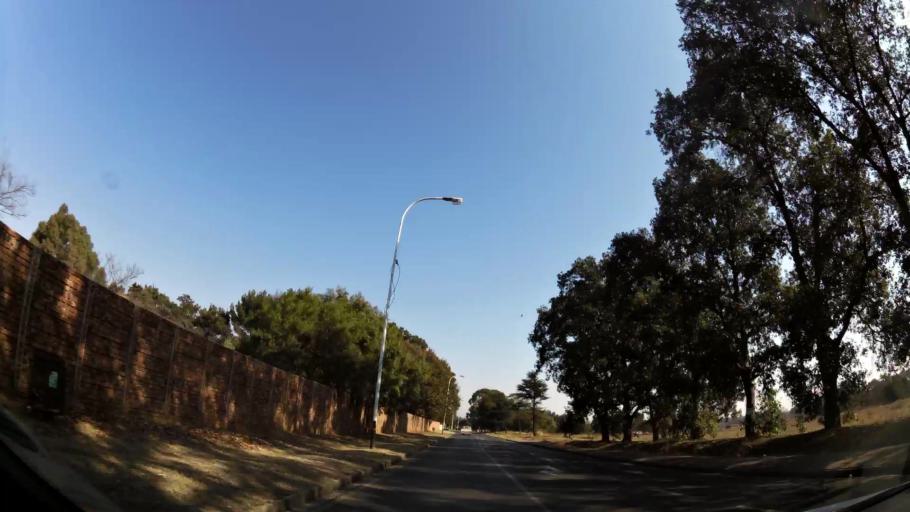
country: ZA
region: Gauteng
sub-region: Ekurhuleni Metropolitan Municipality
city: Boksburg
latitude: -26.2210
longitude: 28.2658
